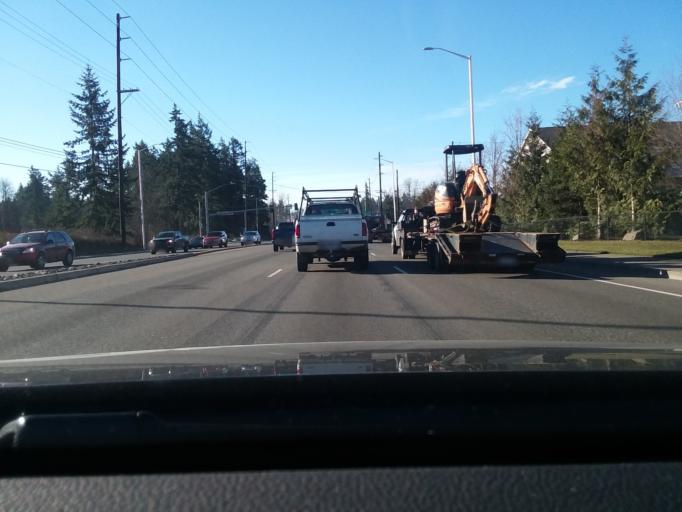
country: US
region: Washington
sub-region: Pierce County
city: Frederickson
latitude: 47.1068
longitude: -122.3577
